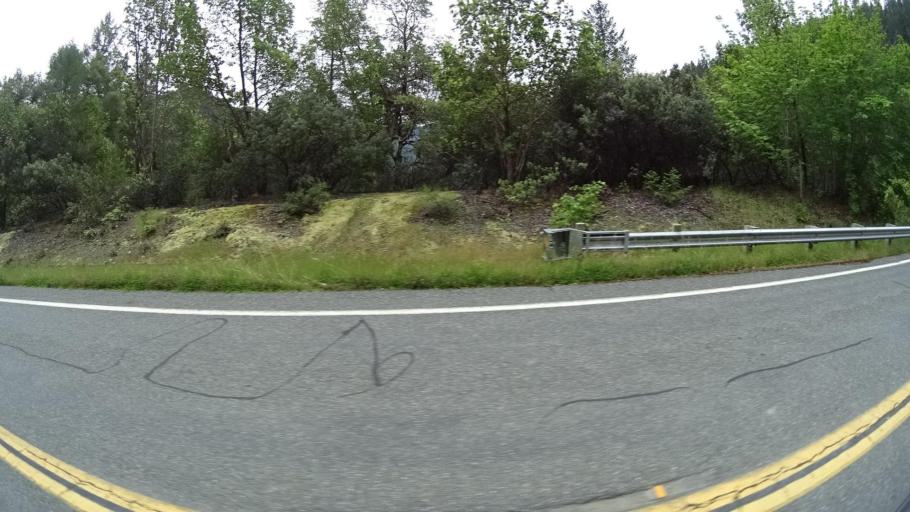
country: US
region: California
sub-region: Humboldt County
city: Willow Creek
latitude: 41.2767
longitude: -123.6055
